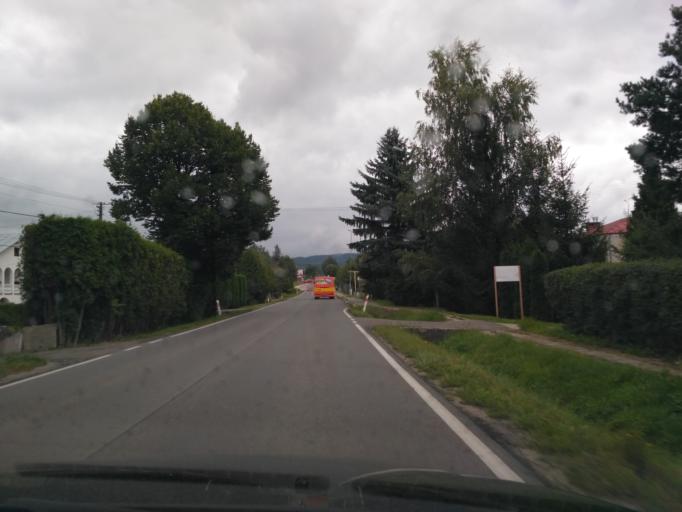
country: PL
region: Subcarpathian Voivodeship
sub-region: Powiat krosnienski
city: Korczyna
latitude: 49.7118
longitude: 21.7932
